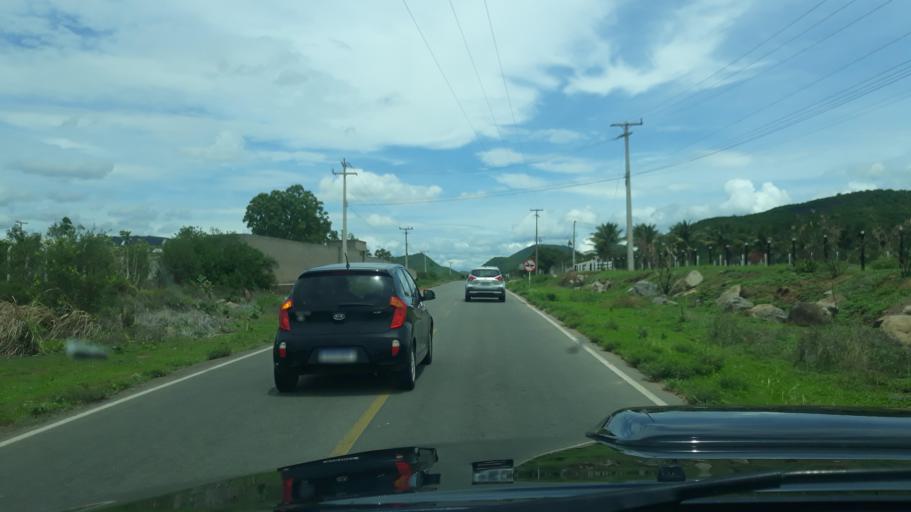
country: BR
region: Bahia
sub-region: Guanambi
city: Guanambi
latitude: -14.2543
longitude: -42.7388
